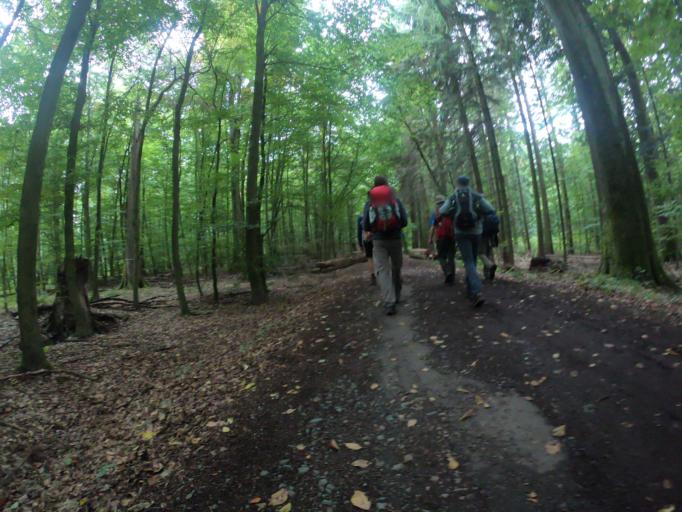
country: DE
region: Hesse
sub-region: Regierungsbezirk Darmstadt
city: Wiesbaden
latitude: 50.1030
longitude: 8.2318
